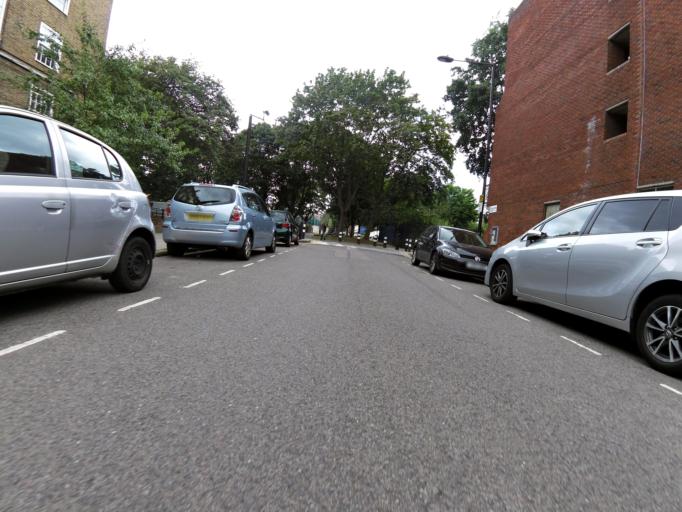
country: GB
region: England
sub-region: Greater London
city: Camden Town
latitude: 51.5321
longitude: -0.1310
